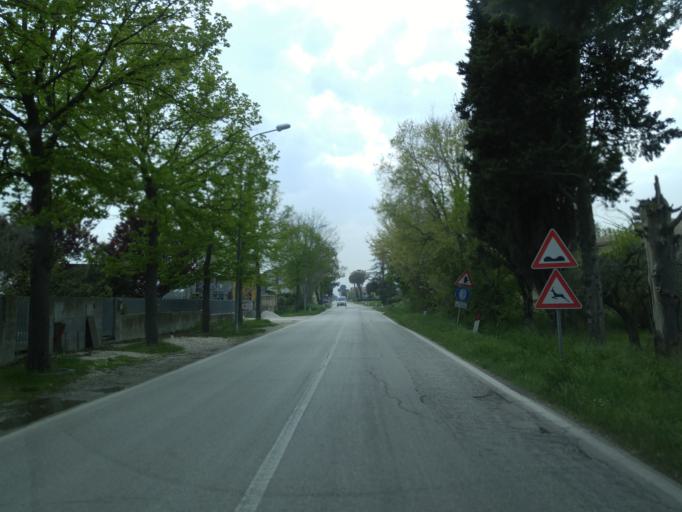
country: IT
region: The Marches
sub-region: Provincia di Pesaro e Urbino
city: Bellocchi
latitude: 43.7864
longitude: 12.9920
